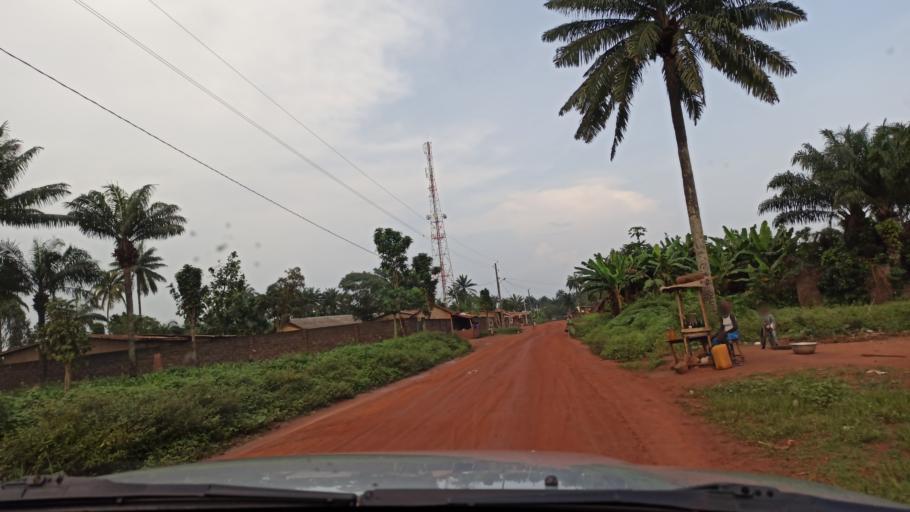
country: BJ
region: Queme
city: Porto-Novo
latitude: 6.4962
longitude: 2.6947
